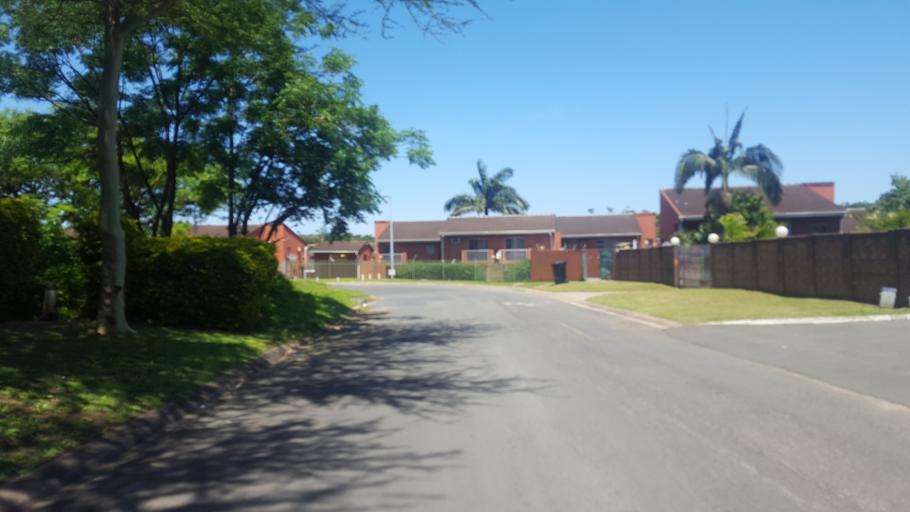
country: ZA
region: KwaZulu-Natal
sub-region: uThungulu District Municipality
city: Richards Bay
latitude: -28.7657
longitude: 32.0664
